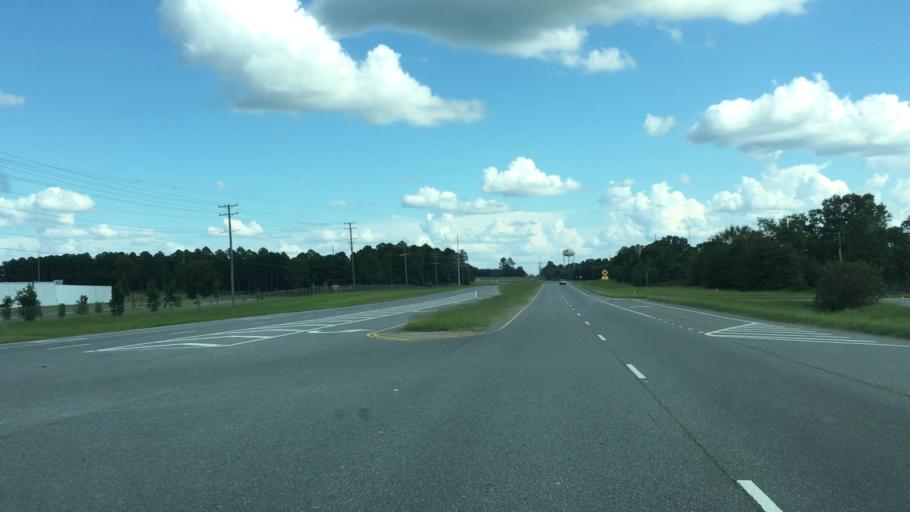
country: US
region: Georgia
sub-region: Laurens County
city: Dublin
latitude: 32.5072
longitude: -82.9468
